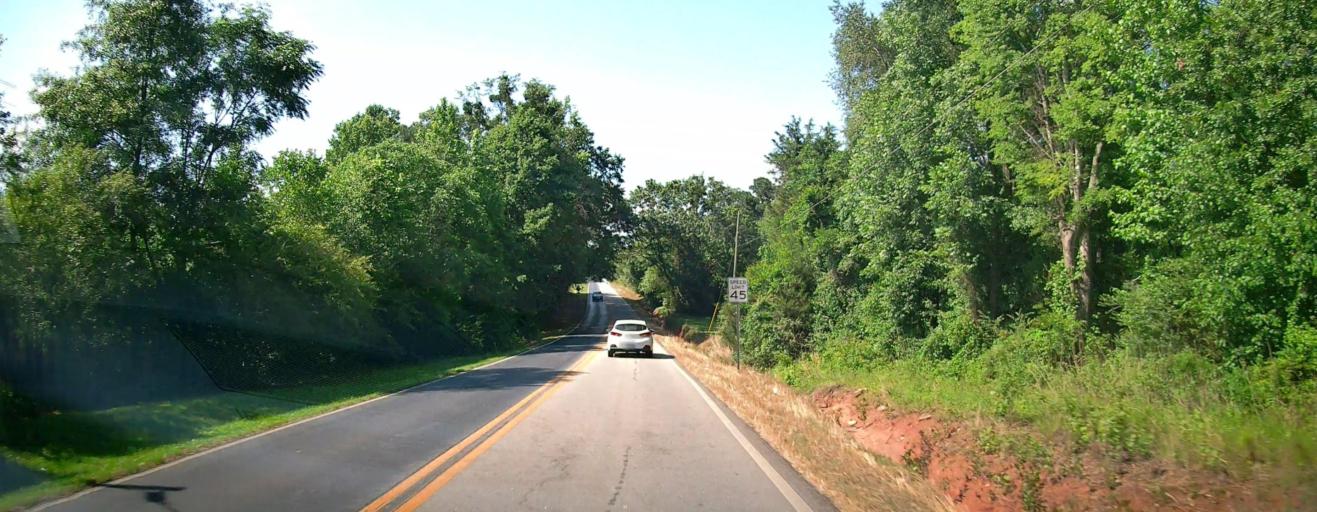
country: US
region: Georgia
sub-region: Spalding County
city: East Griffin
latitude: 33.2858
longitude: -84.1898
